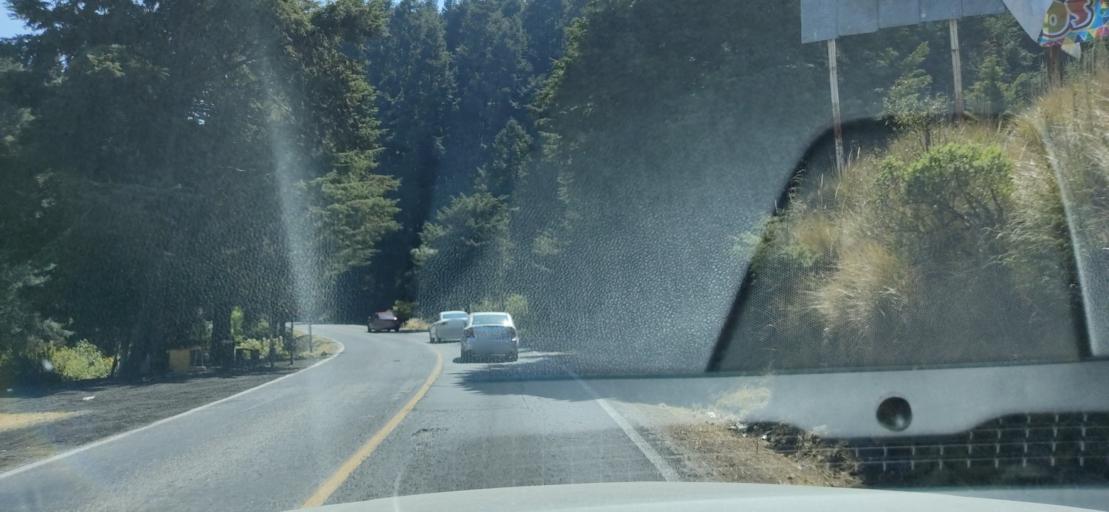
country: MX
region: Mexico
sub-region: Ocoyoacac
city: San Jeronimo Acazulco
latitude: 19.2762
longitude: -99.3793
